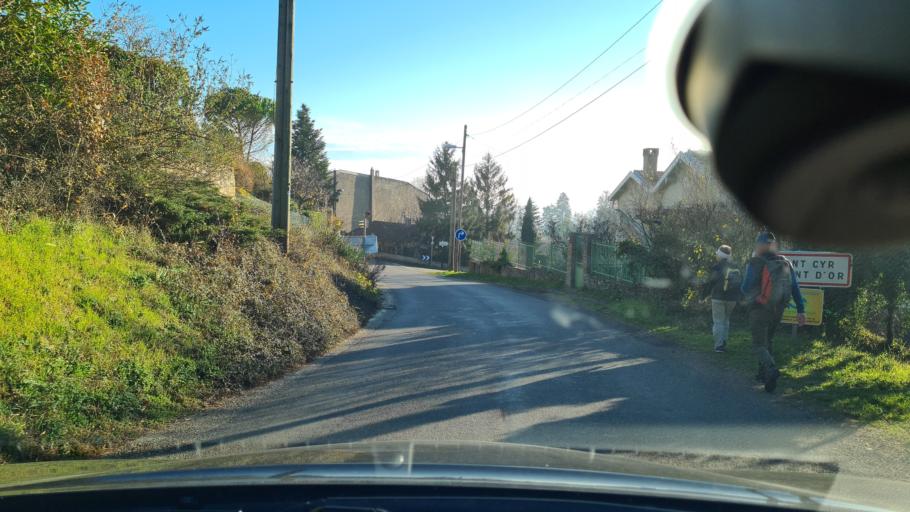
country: FR
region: Rhone-Alpes
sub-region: Departement du Rhone
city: Fontaines-sur-Saone
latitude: 45.8269
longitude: 4.8100
